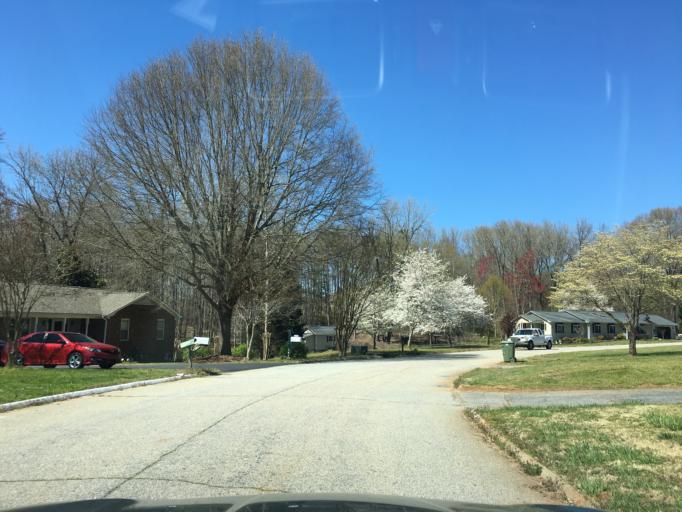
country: US
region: South Carolina
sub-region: Spartanburg County
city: Wellford
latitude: 34.8817
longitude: -82.0676
